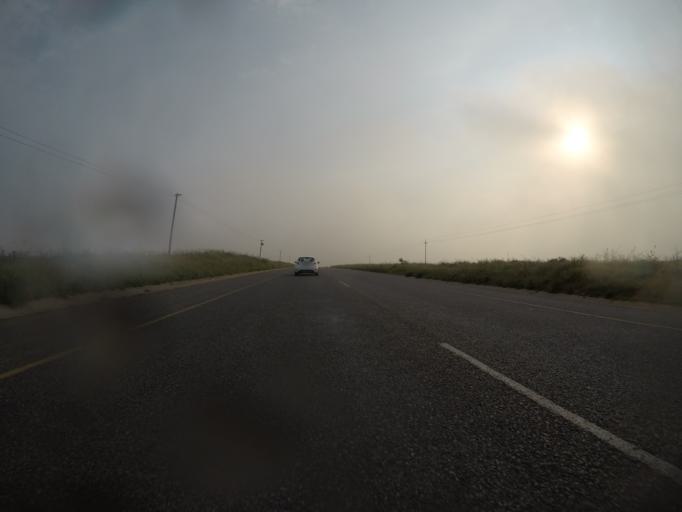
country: ZA
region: Western Cape
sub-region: West Coast District Municipality
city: Malmesbury
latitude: -33.6510
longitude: 18.7103
